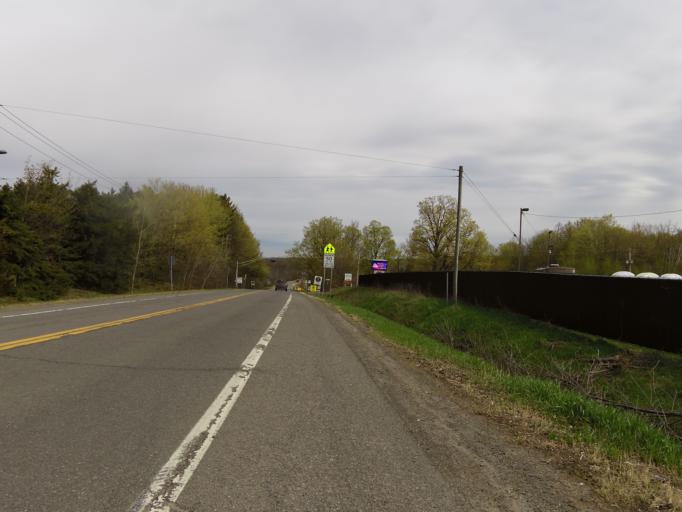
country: CA
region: Quebec
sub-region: Monteregie
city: Hudson
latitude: 45.4803
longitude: -74.1286
